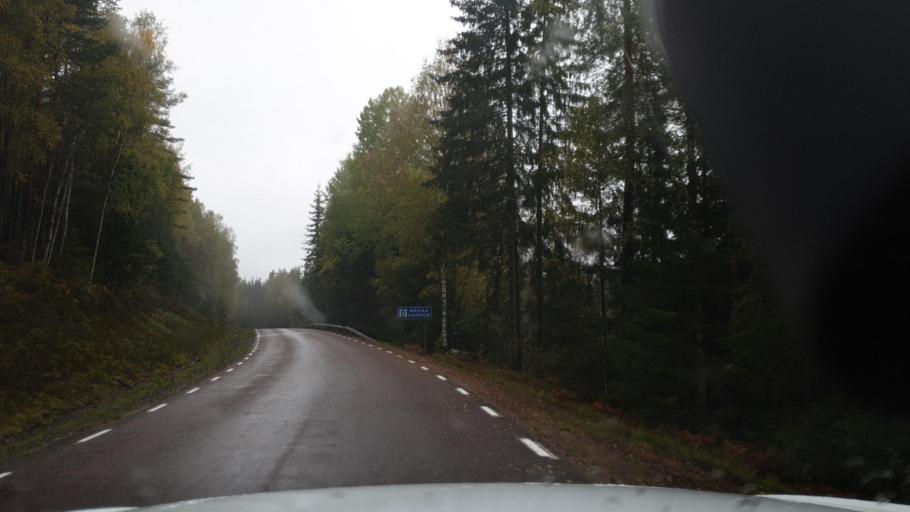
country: SE
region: Vaermland
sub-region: Grums Kommun
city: Grums
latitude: 59.5080
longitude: 12.8705
